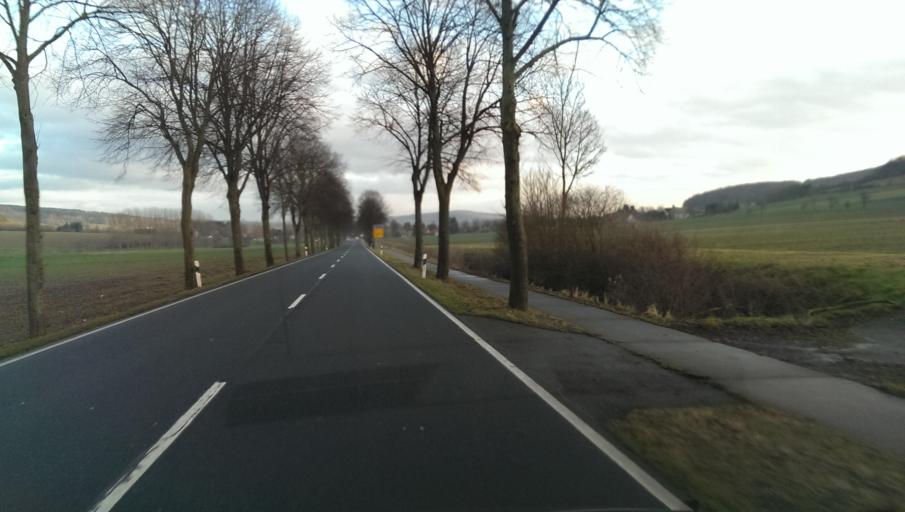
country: DE
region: Lower Saxony
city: Eimen
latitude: 51.8814
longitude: 9.7688
